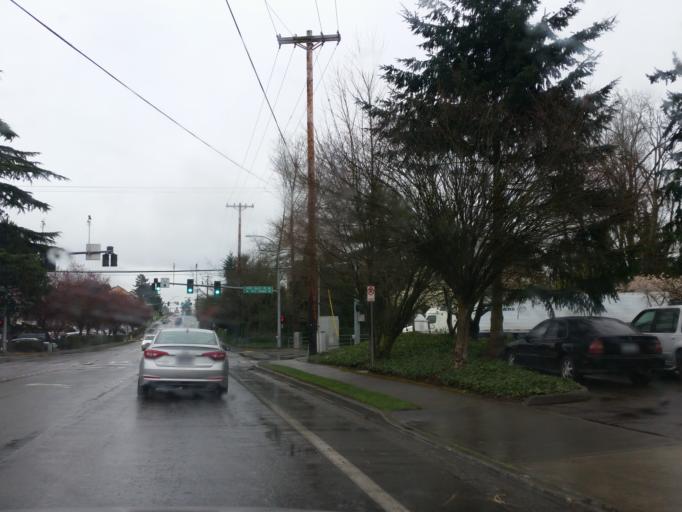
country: US
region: Washington
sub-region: Snohomish County
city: Lynnwood
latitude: 47.8174
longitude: -122.3013
